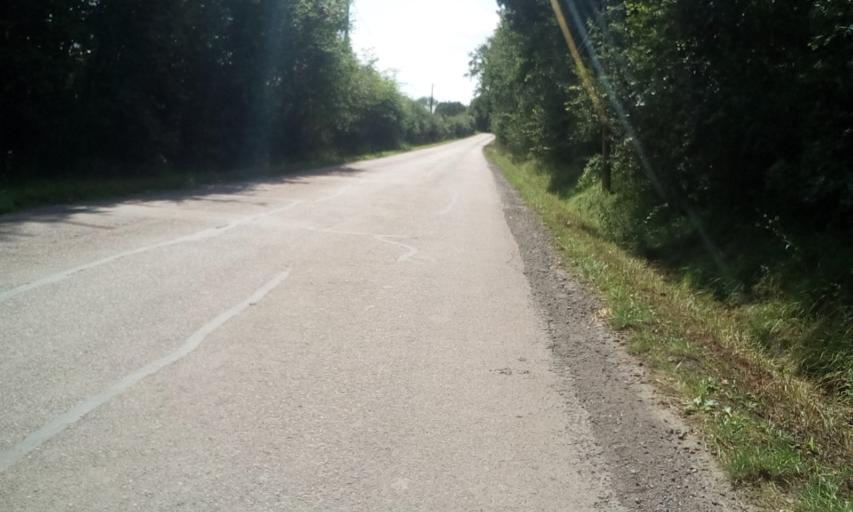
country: FR
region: Lower Normandy
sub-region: Departement du Calvados
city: Argences
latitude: 49.1396
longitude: -0.1551
